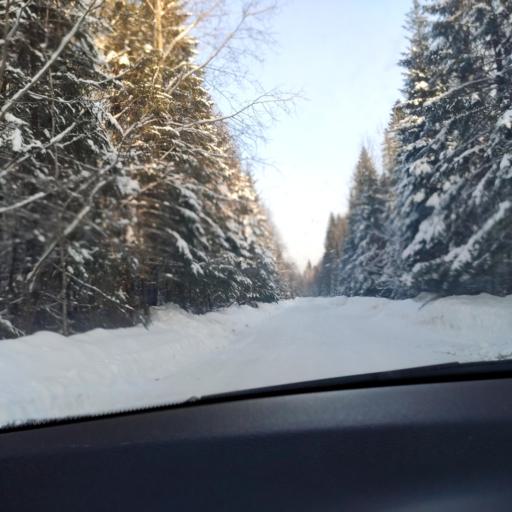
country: RU
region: Perm
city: Kondratovo
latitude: 58.0821
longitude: 56.1314
